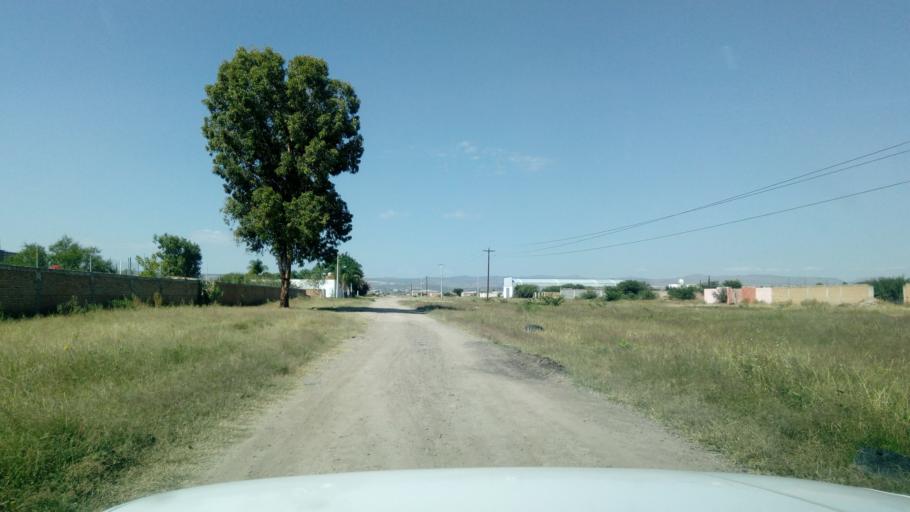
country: MX
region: Durango
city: Victoria de Durango
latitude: 23.9827
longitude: -104.6675
